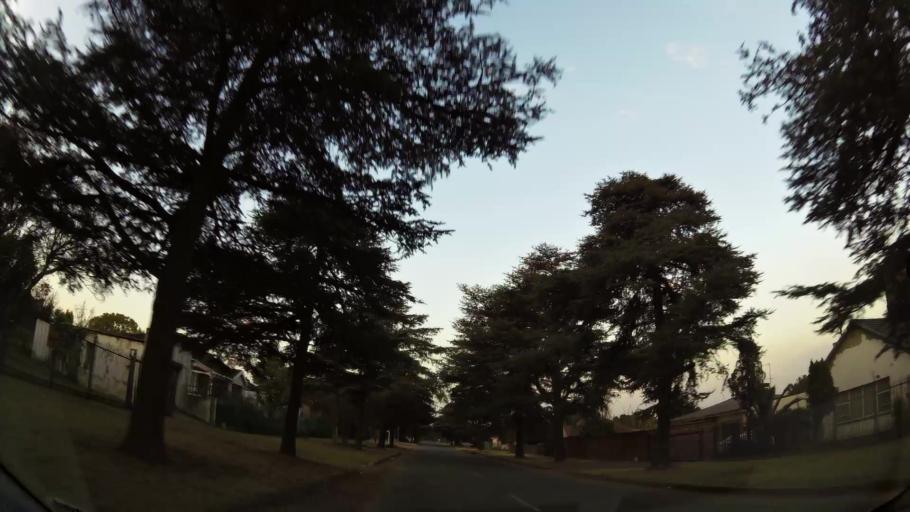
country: ZA
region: Gauteng
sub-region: Ekurhuleni Metropolitan Municipality
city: Benoni
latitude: -26.1785
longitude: 28.3165
